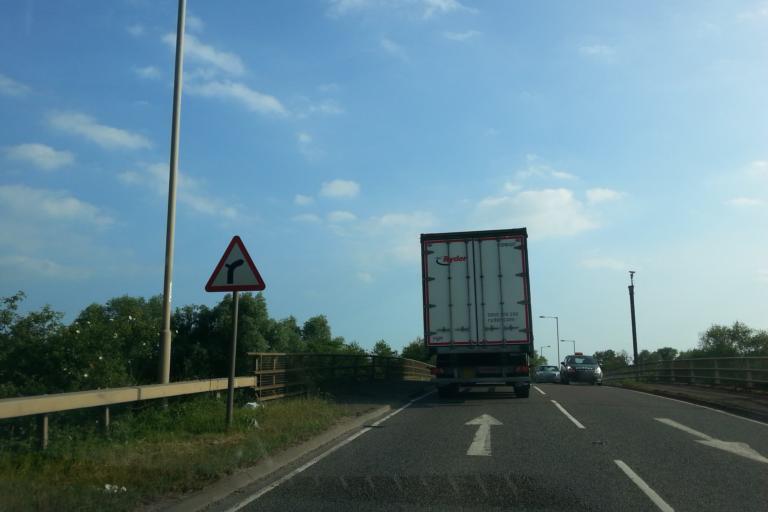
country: GB
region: England
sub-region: Cambridgeshire
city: Hemingford Grey
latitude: 52.3027
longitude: -0.0895
